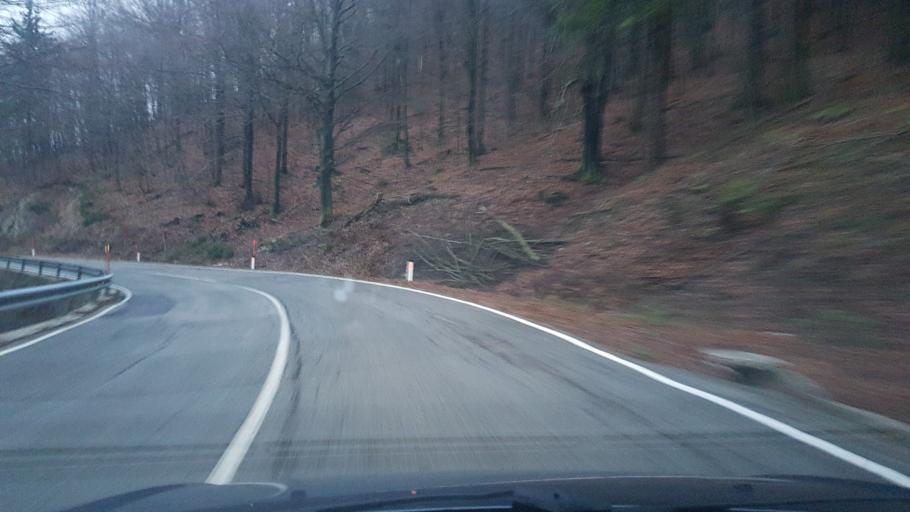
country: SI
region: Idrija
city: Idrija
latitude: 45.9206
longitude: 14.0422
